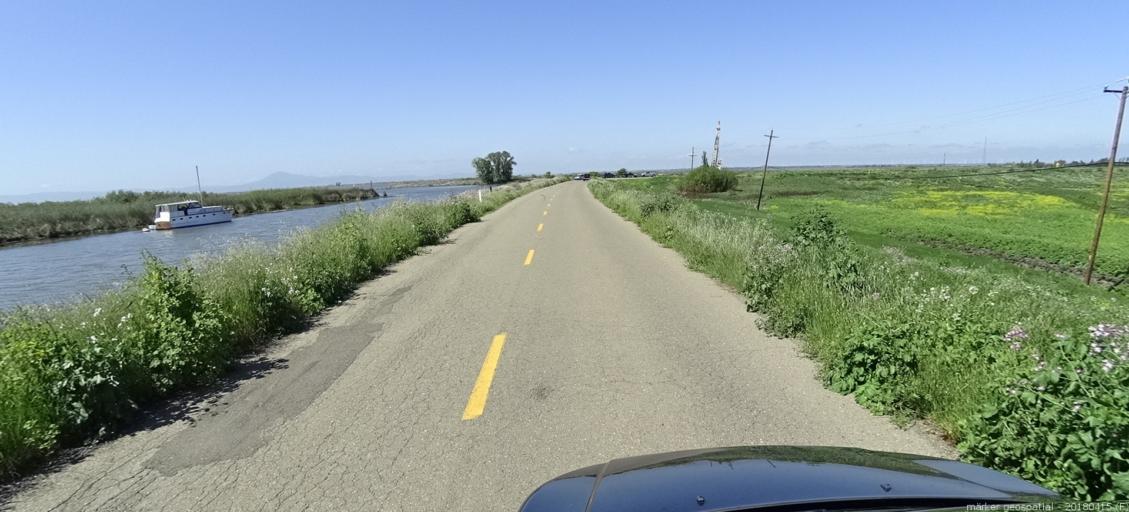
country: US
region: California
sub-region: Solano County
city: Rio Vista
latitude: 38.1083
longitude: -121.6106
